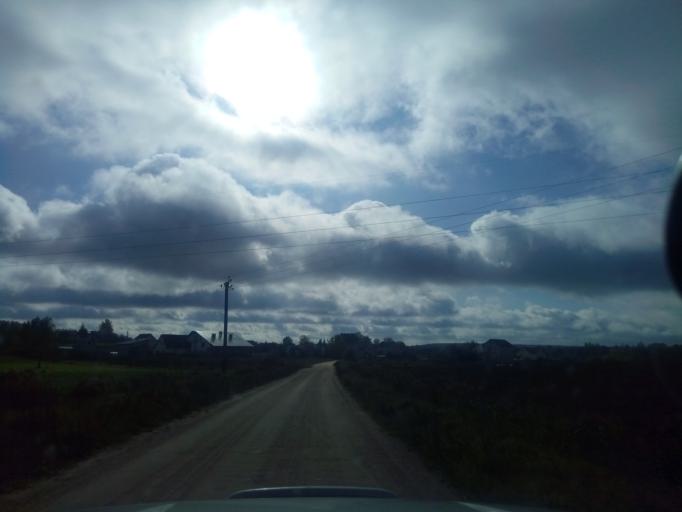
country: BY
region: Minsk
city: Zaslawye
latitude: 54.0189
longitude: 27.2903
